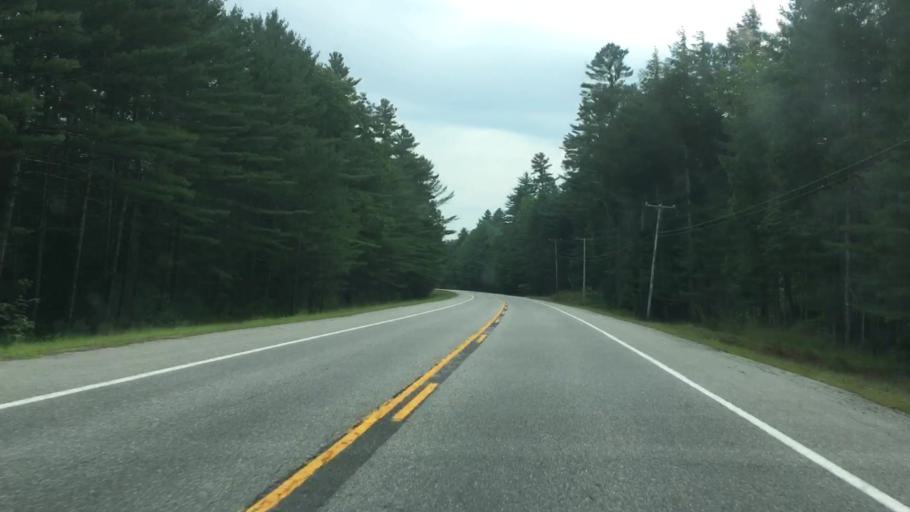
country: US
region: Maine
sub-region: Oxford County
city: Bethel
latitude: 44.4626
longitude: -70.8033
